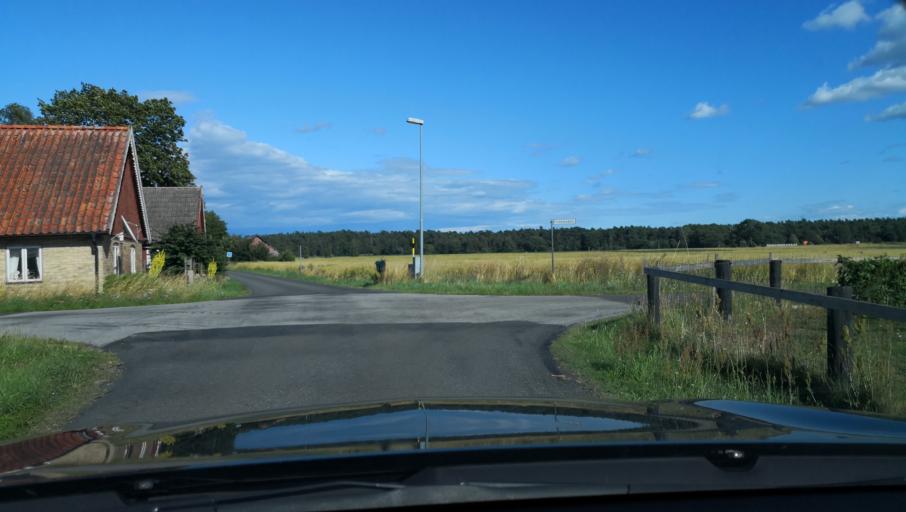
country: SE
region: Skane
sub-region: Kristianstads Kommun
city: Degeberga
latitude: 55.8149
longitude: 14.1887
